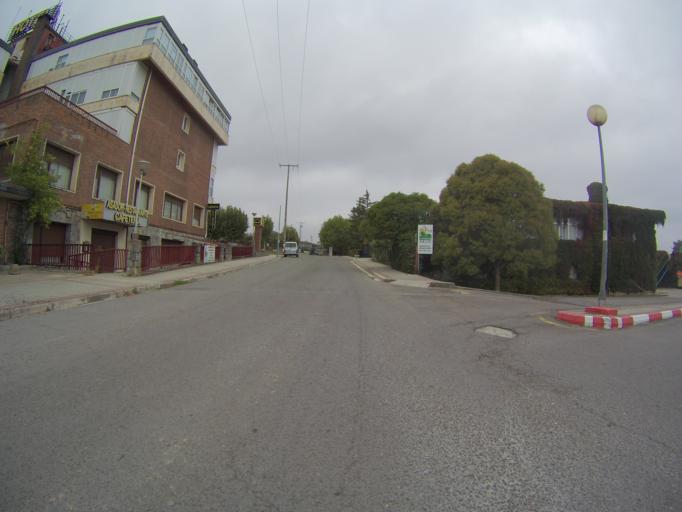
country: ES
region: Navarre
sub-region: Provincia de Navarra
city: Ayegui
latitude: 42.6470
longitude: -2.0557
